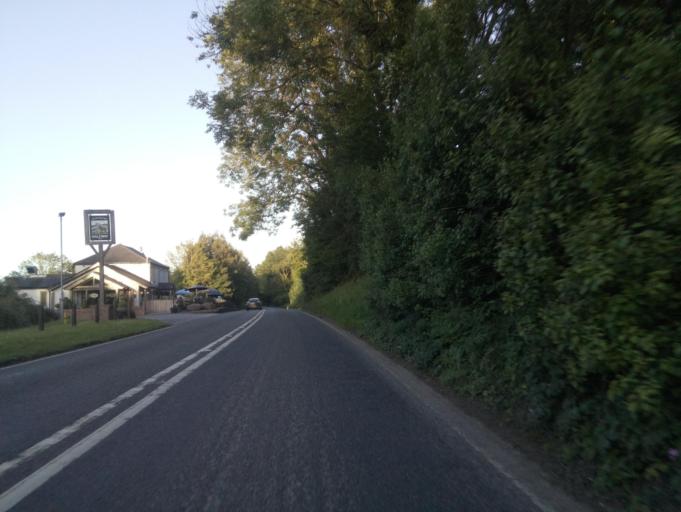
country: GB
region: England
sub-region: Devon
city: Bovey Tracey
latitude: 50.5346
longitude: -3.6897
